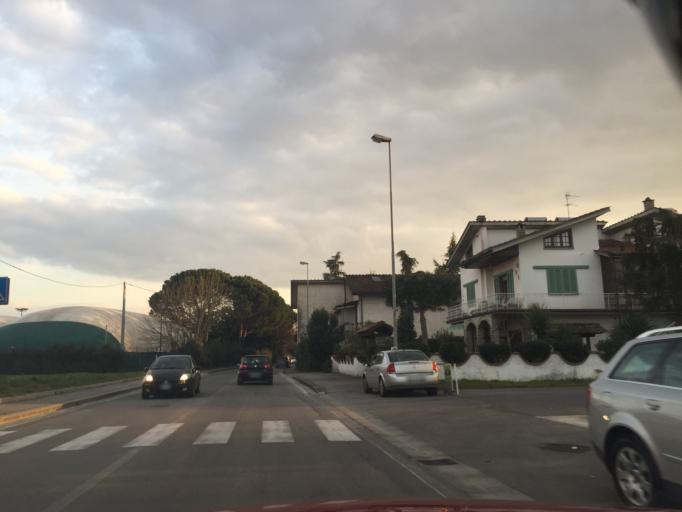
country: IT
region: Tuscany
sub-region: Provincia di Pistoia
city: Borgo a Buggiano
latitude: 43.8672
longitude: 10.7399
